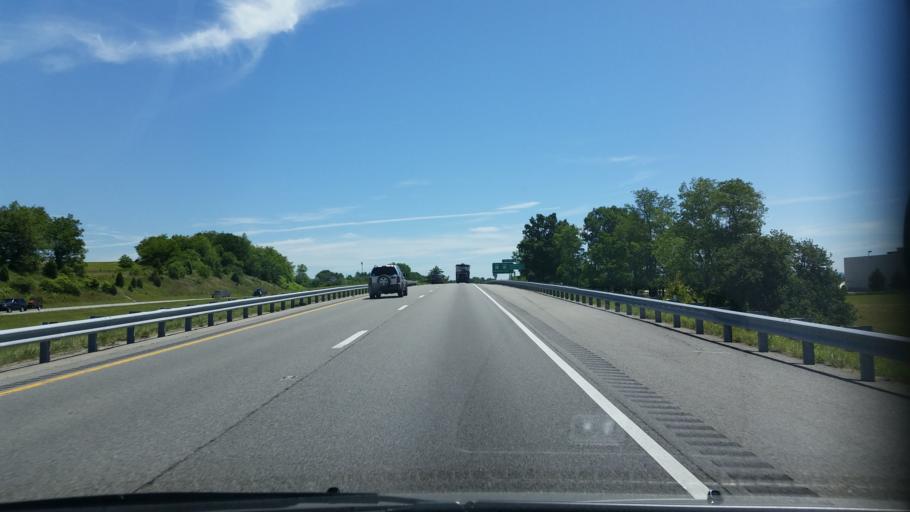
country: US
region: Virginia
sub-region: Wythe County
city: Wytheville
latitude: 36.9575
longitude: -81.1069
